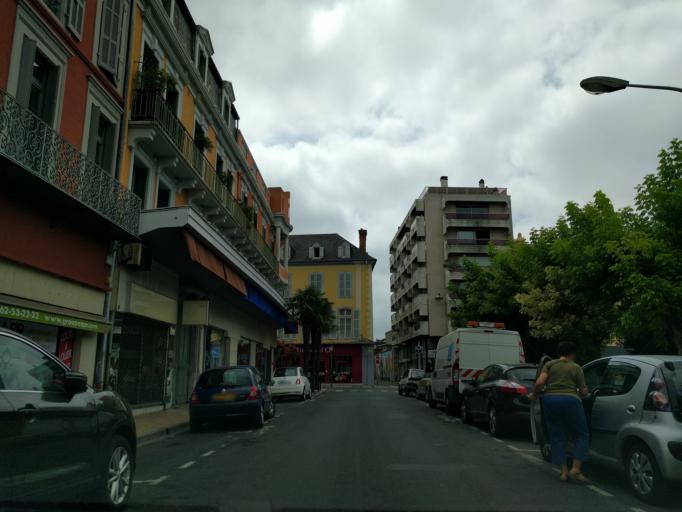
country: FR
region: Midi-Pyrenees
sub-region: Departement des Hautes-Pyrenees
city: Tarbes
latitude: 43.2325
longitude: 0.0784
